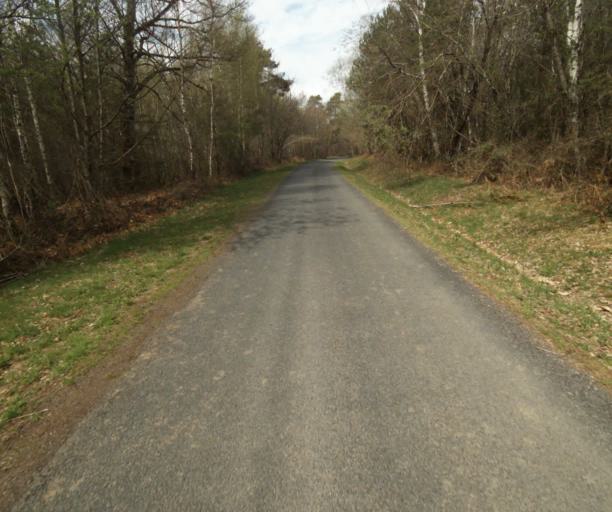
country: FR
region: Limousin
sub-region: Departement de la Correze
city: Argentat
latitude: 45.1976
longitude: 1.9087
